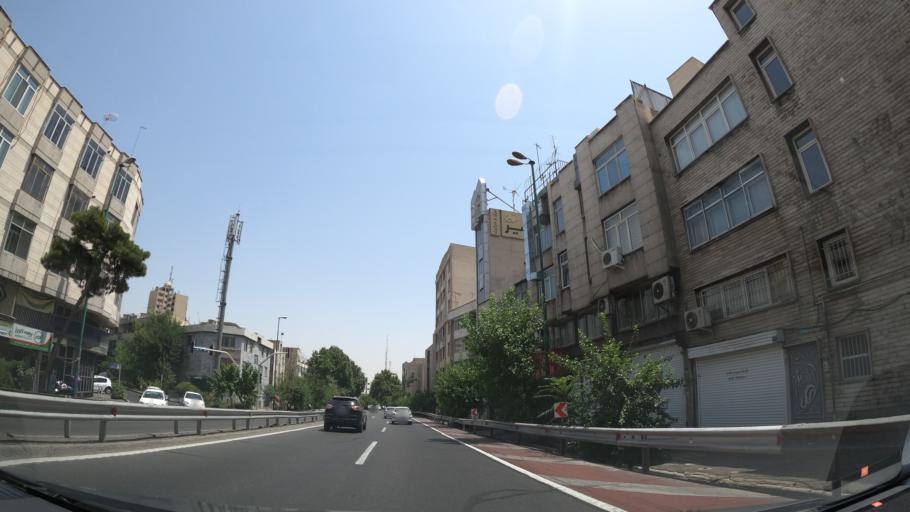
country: IR
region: Tehran
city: Tehran
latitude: 35.7221
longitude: 51.4254
